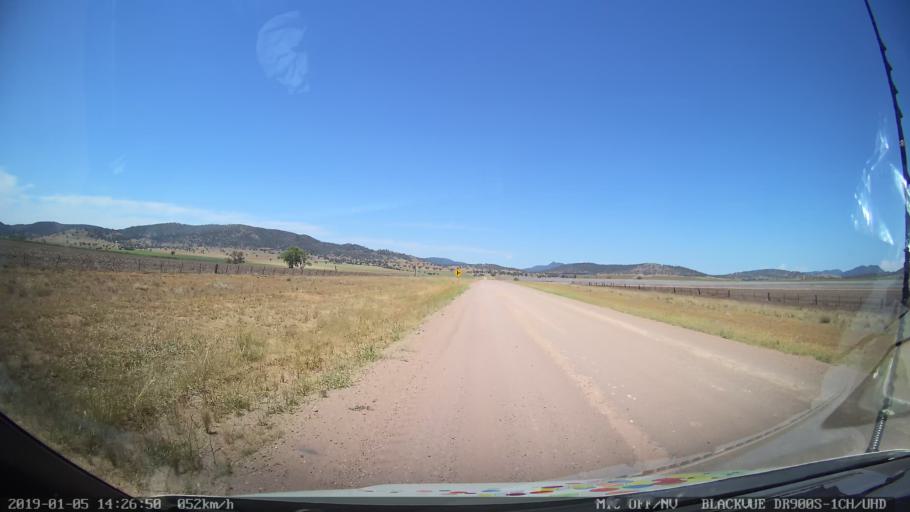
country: AU
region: New South Wales
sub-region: Liverpool Plains
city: Quirindi
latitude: -31.2366
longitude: 150.5606
